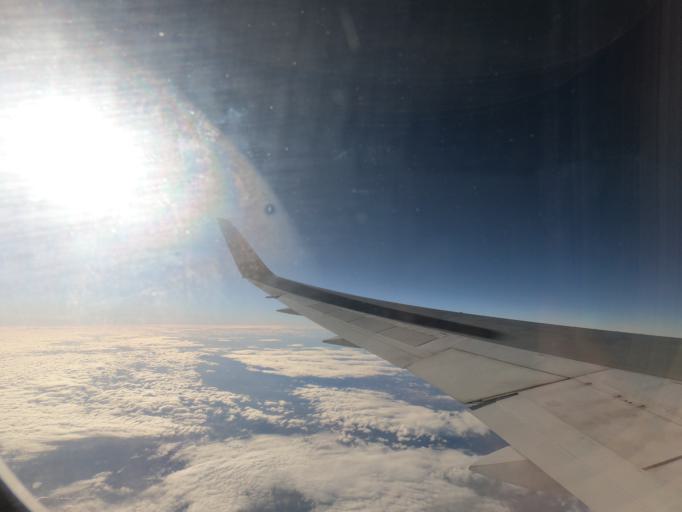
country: GB
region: England
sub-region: City and Borough of Wakefield
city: Ferrybridge
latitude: 53.6991
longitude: -1.2786
